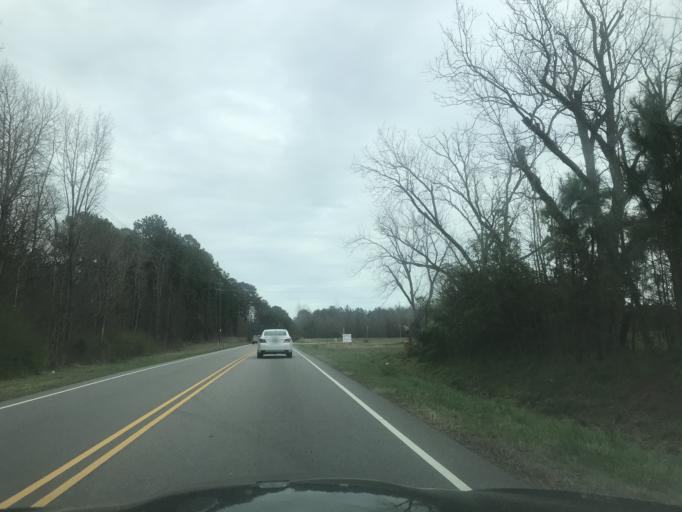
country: US
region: North Carolina
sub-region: Franklin County
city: Louisburg
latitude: 36.0856
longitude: -78.3529
